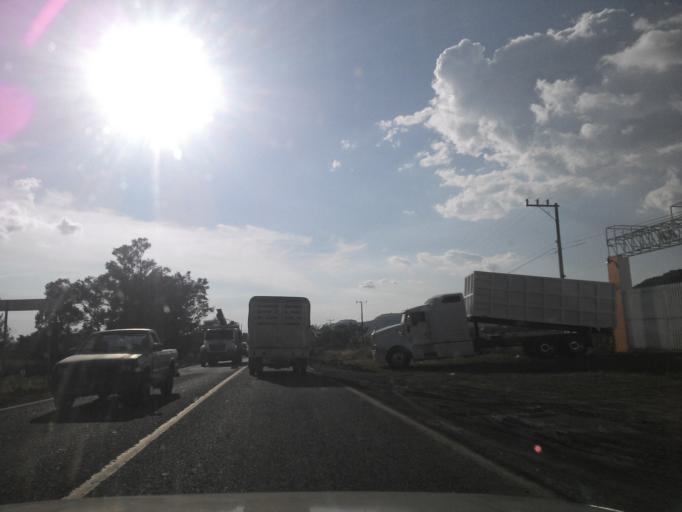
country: MX
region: Jalisco
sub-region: Atotonilco el Alto
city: San Francisco de Asis
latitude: 20.5426
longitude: -102.5934
